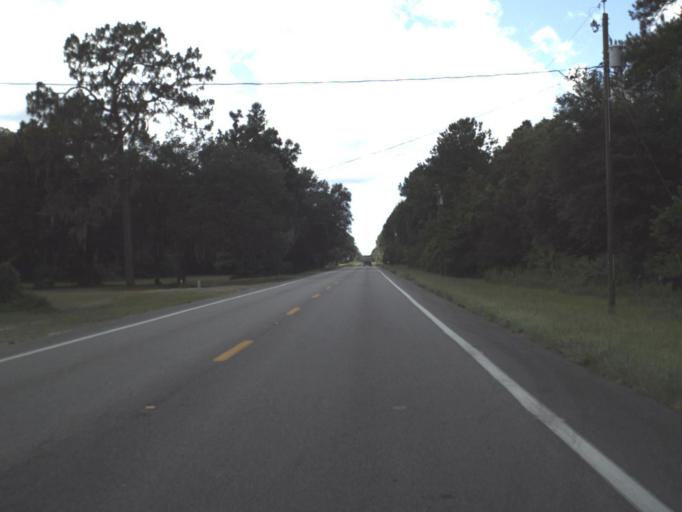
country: US
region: Florida
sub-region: Taylor County
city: Perry
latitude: 30.1026
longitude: -83.6137
